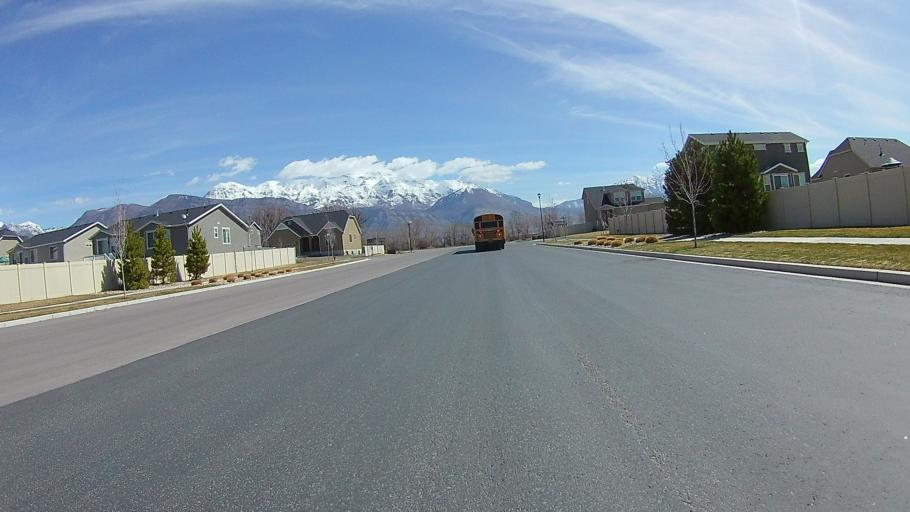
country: US
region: Utah
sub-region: Utah County
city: American Fork
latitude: 40.3626
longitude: -111.8031
